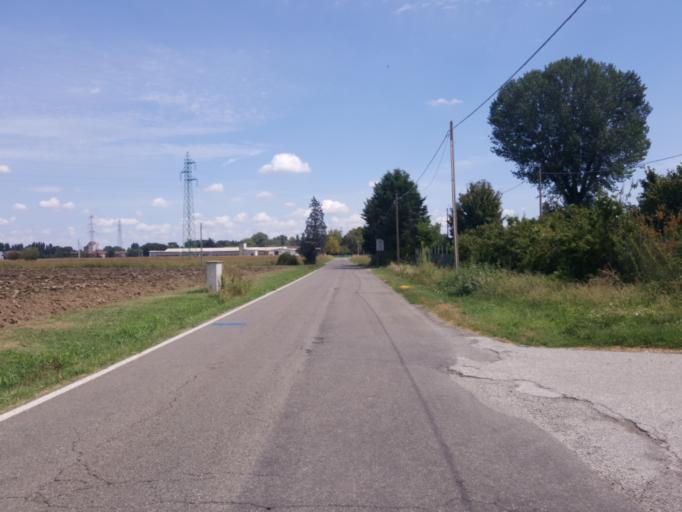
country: IT
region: Emilia-Romagna
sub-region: Provincia di Bologna
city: Anzola dell'Emilia
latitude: 44.5263
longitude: 11.2151
